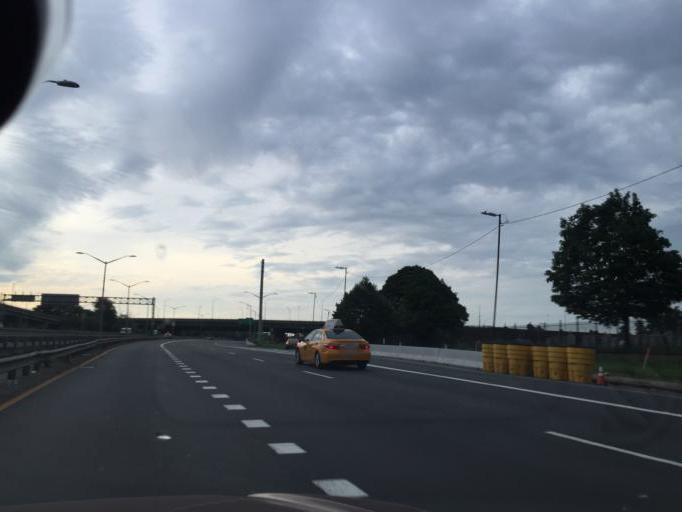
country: US
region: New York
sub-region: Queens County
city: Long Island City
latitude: 40.7356
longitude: -73.9254
